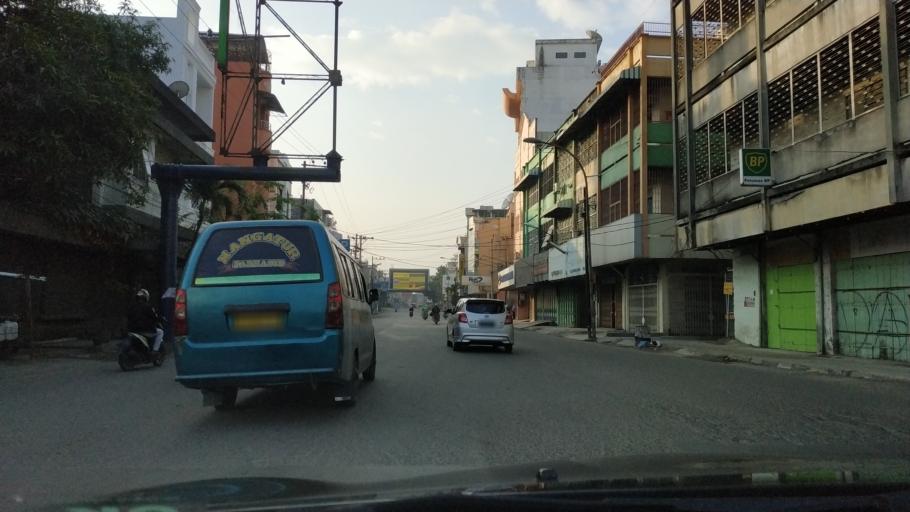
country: ID
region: North Sumatra
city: Medan
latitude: 3.5889
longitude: 98.6904
